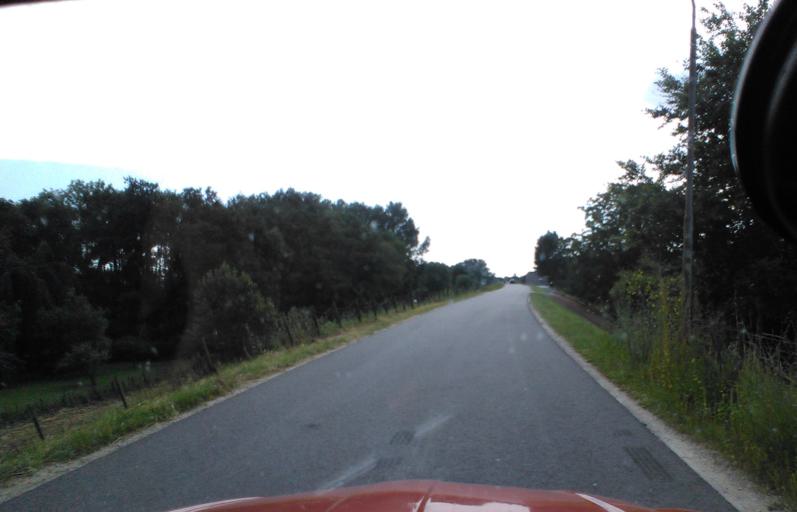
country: NL
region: South Holland
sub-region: Gemeente Leerdam
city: Leerdam
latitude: 51.9083
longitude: 5.1267
